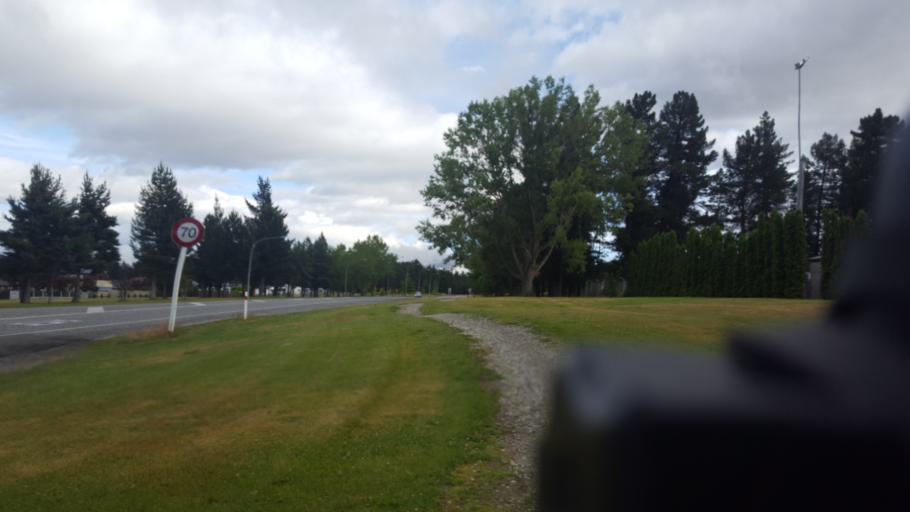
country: NZ
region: Otago
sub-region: Queenstown-Lakes District
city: Wanaka
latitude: -45.2437
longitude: 169.3789
